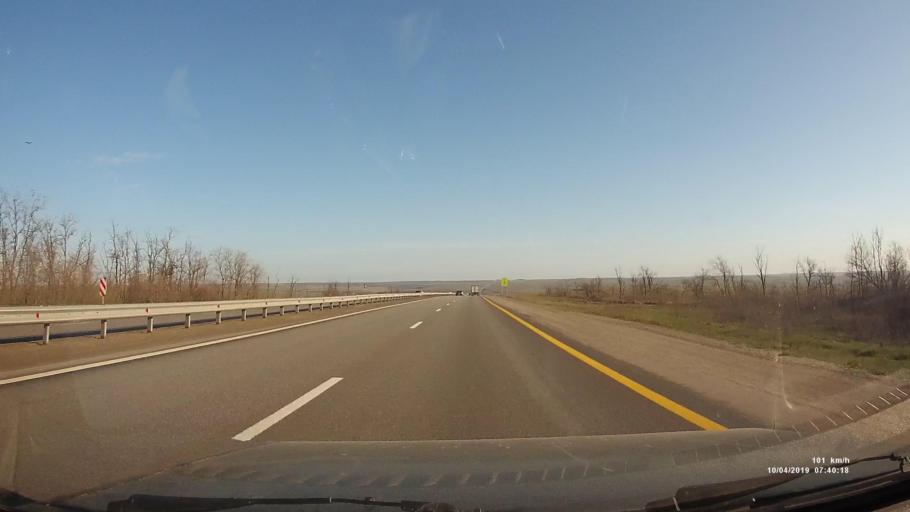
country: RU
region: Rostov
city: Likhoy
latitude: 48.1176
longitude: 40.2593
